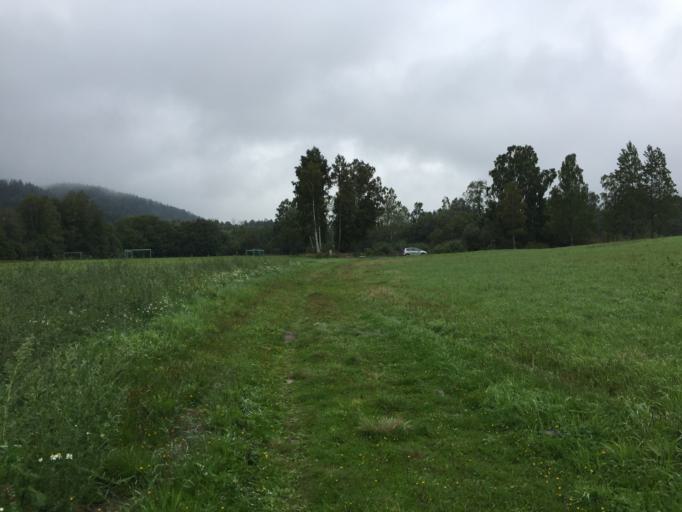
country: NO
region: Akershus
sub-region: Baerum
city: Lysaker
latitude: 59.9835
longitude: 10.6198
